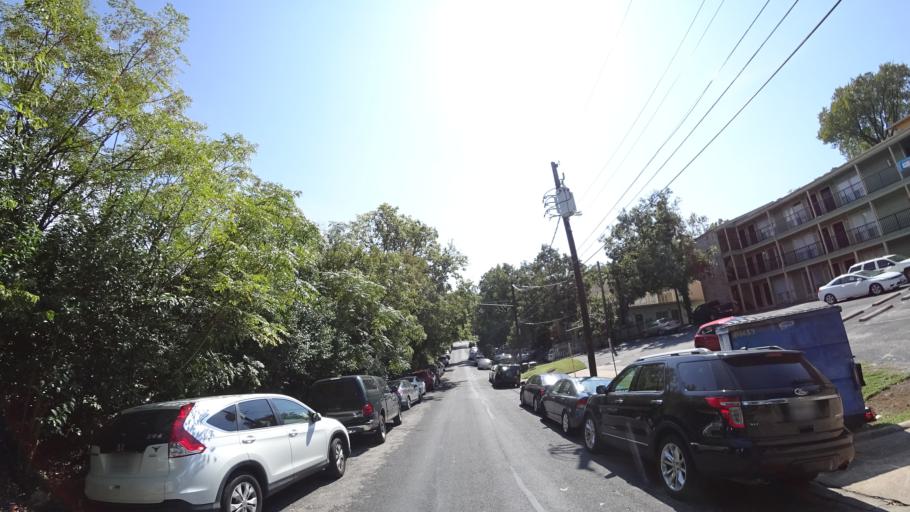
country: US
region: Texas
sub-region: Travis County
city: Austin
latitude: 30.2938
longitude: -97.7401
